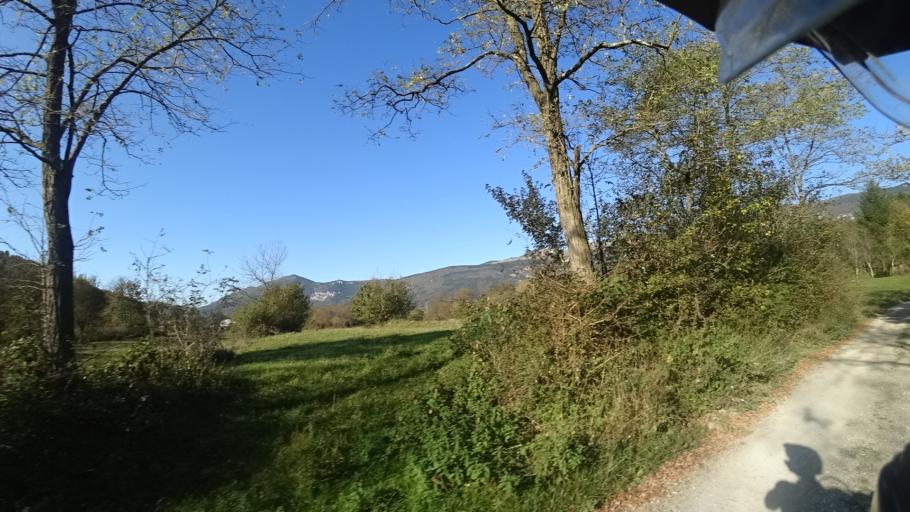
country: HR
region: Primorsko-Goranska
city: Klana
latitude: 45.5084
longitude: 14.3480
